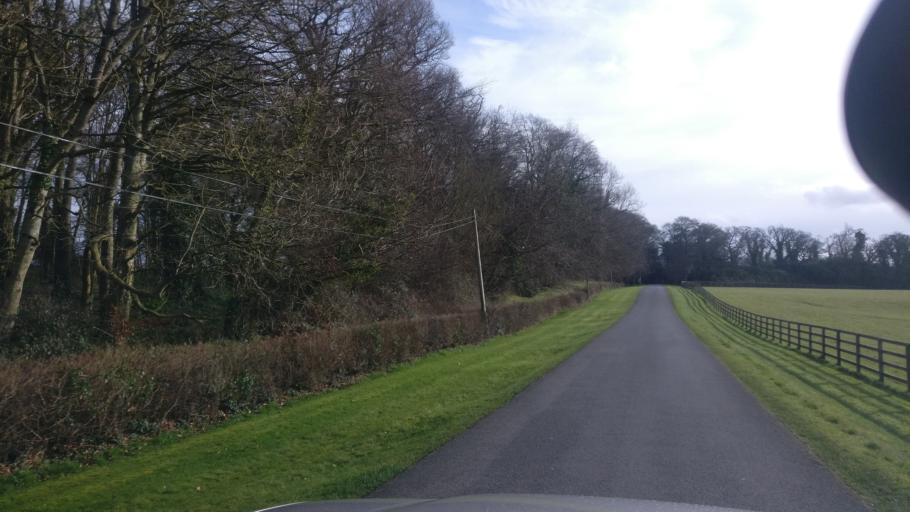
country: IE
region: Leinster
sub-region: Kilkenny
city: Thomastown
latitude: 52.5304
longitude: -7.1717
